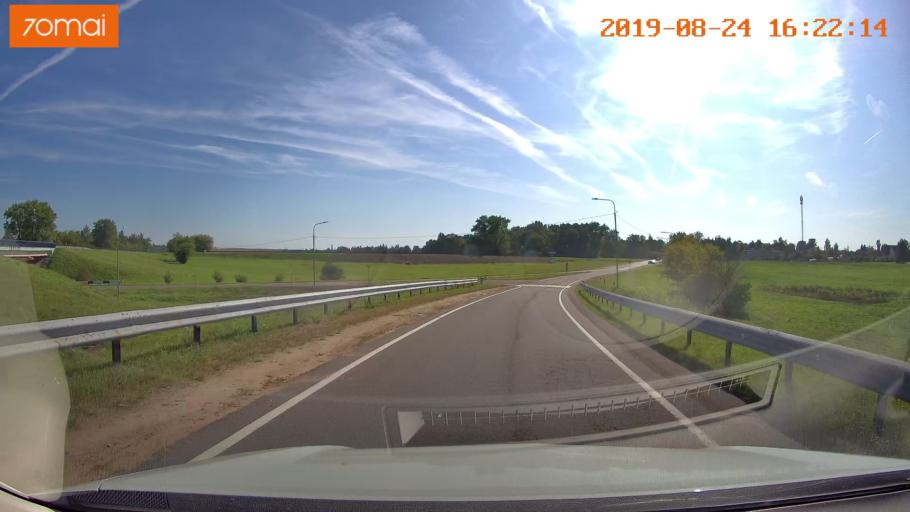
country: BY
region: Minsk
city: Samakhvalavichy
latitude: 53.6363
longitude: 27.4657
